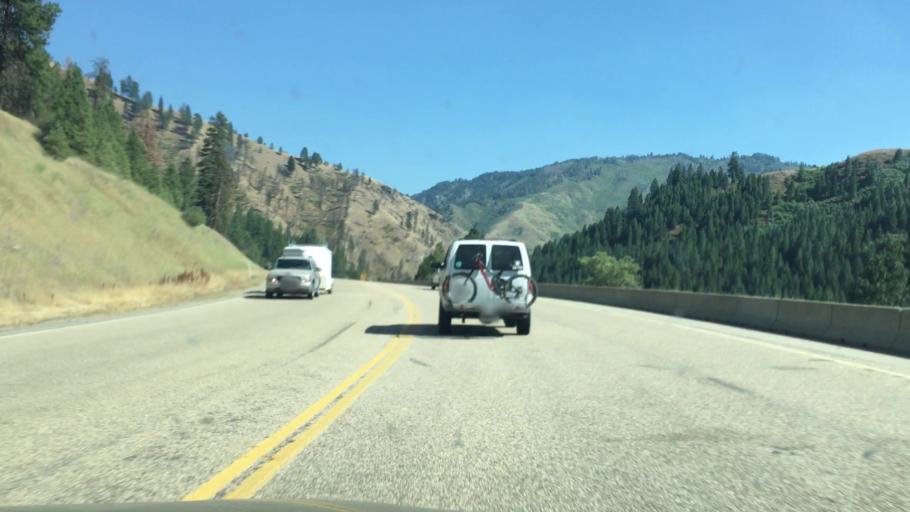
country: US
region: Idaho
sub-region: Boise County
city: Idaho City
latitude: 44.1134
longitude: -116.1049
